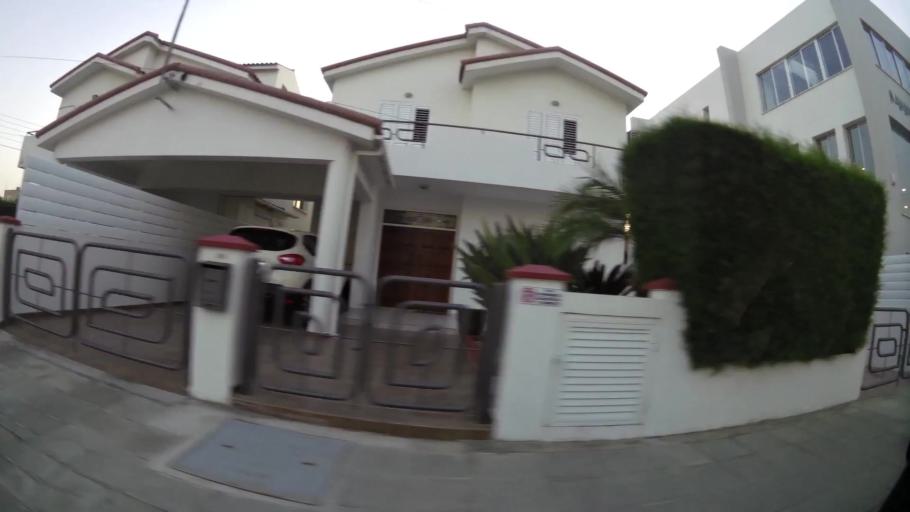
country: CY
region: Larnaka
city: Larnaca
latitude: 34.9148
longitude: 33.5963
